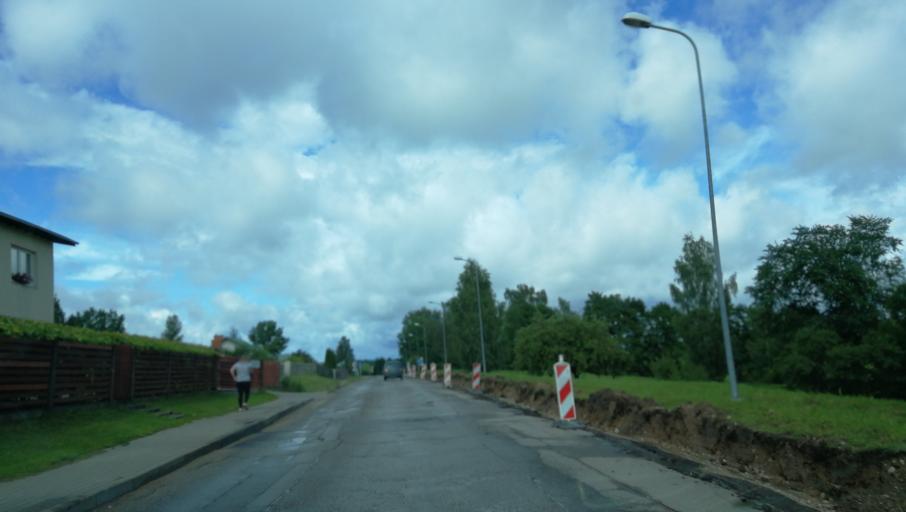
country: LV
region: Cesu Rajons
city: Cesis
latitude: 57.3137
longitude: 25.2580
